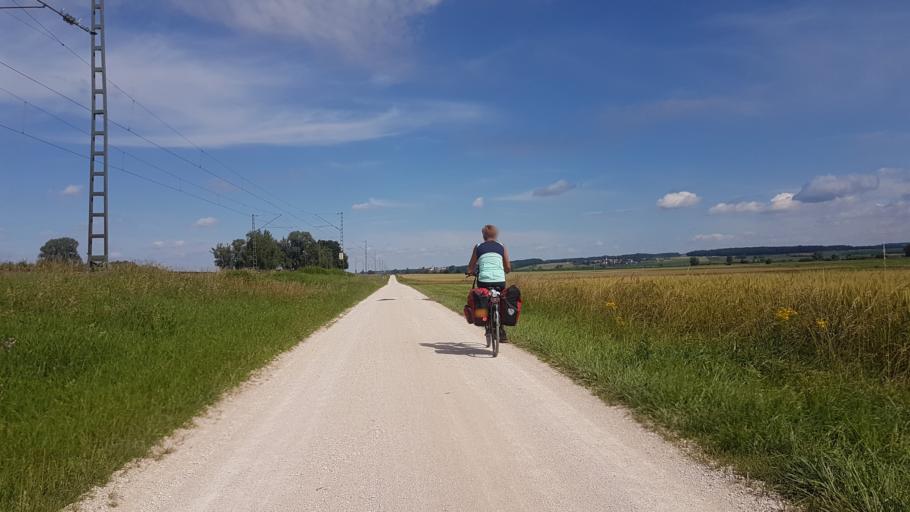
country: DE
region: Bavaria
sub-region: Regierungsbezirk Mittelfranken
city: Markt Berolzheim
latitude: 49.0229
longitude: 10.8486
